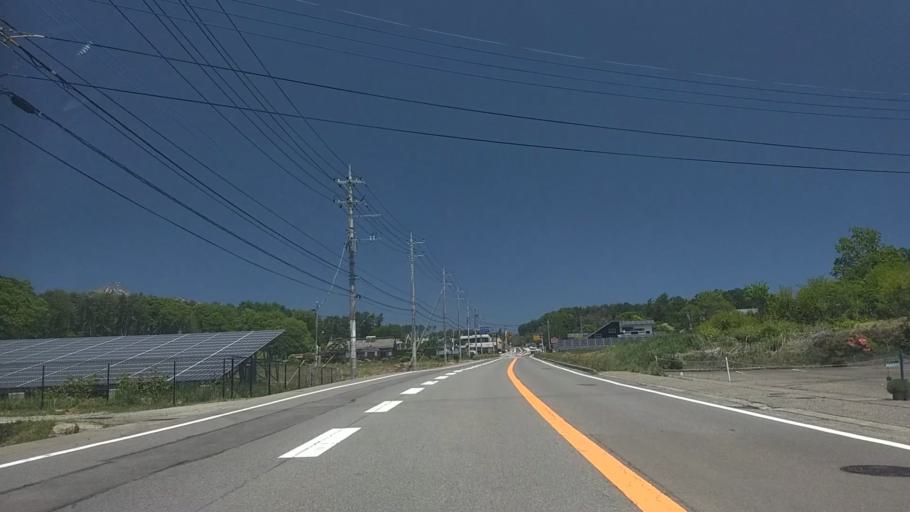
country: JP
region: Yamanashi
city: Nirasaki
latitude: 35.8804
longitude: 138.4397
